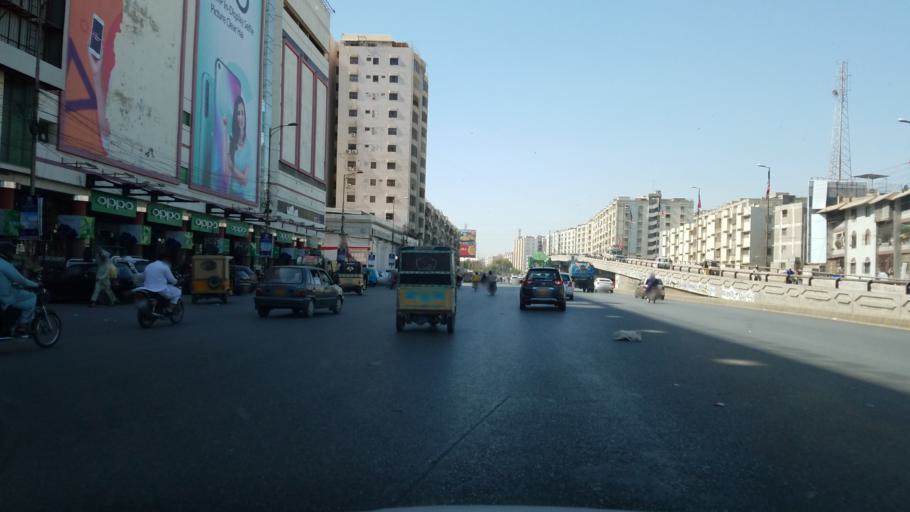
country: PK
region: Sindh
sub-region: Karachi District
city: Karachi
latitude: 24.9027
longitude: 67.1148
